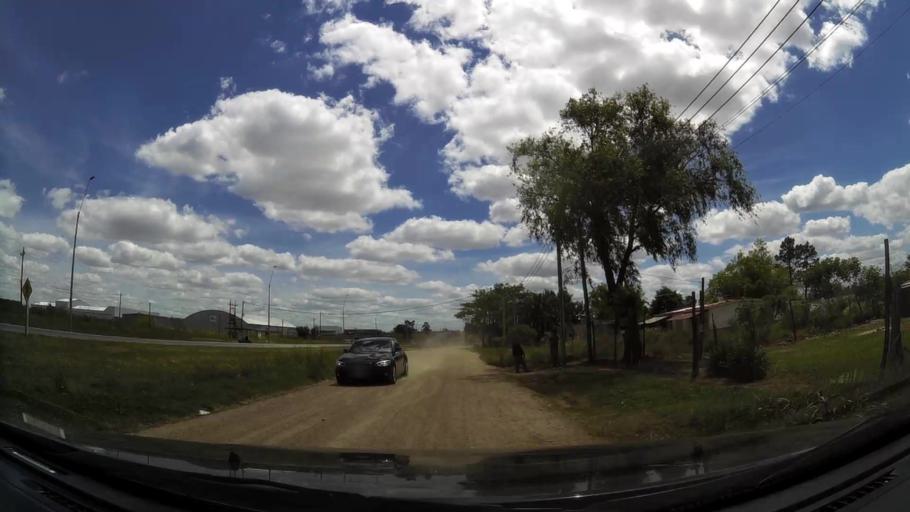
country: UY
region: Canelones
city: Colonia Nicolich
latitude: -34.7950
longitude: -56.0027
